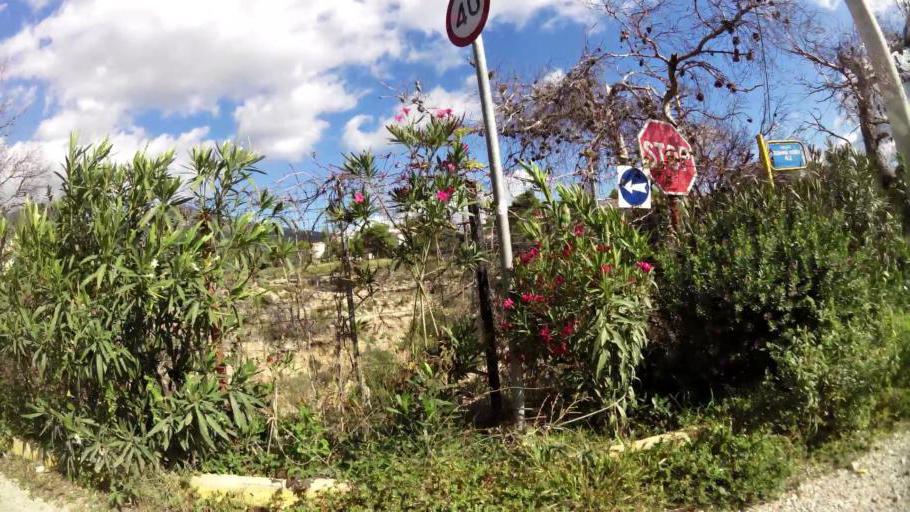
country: GR
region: Attica
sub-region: Nomarchia Anatolikis Attikis
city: Thrakomakedones
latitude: 38.1242
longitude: 23.7505
